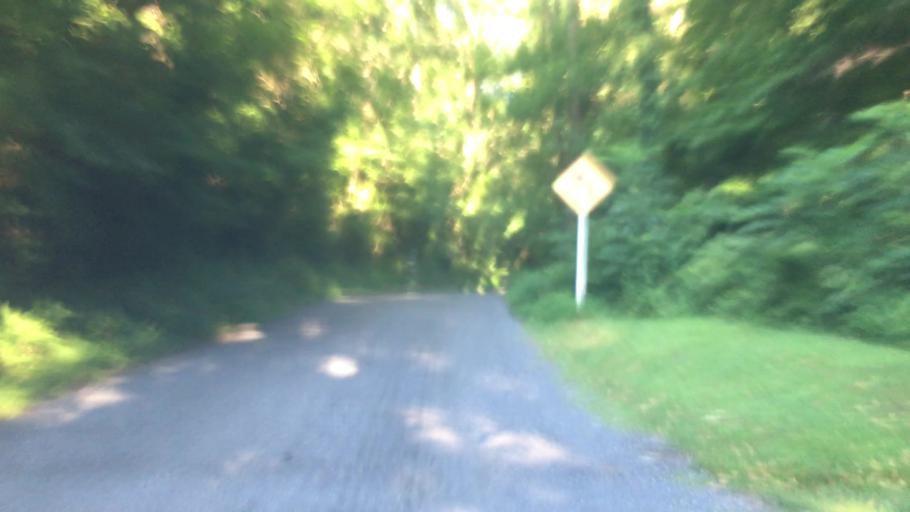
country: US
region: Maryland
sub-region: Frederick County
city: Point of Rocks
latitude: 39.3048
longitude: -77.5525
